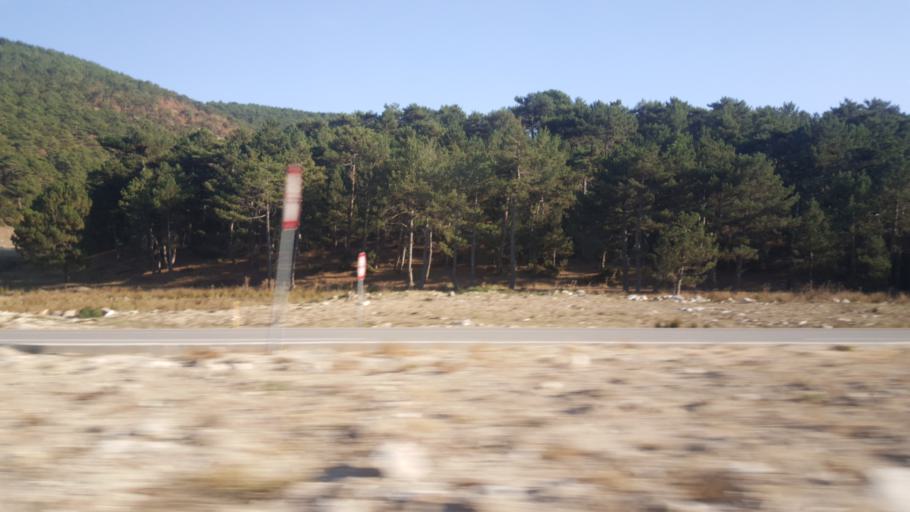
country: TR
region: Afyonkarahisar
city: Ihsaniye
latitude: 39.0995
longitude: 30.5773
